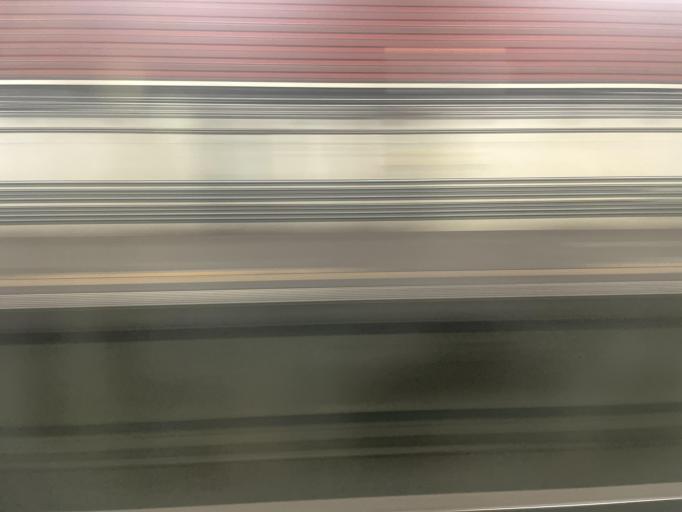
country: JP
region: Hyogo
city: Takarazuka
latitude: 34.8578
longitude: 135.3037
